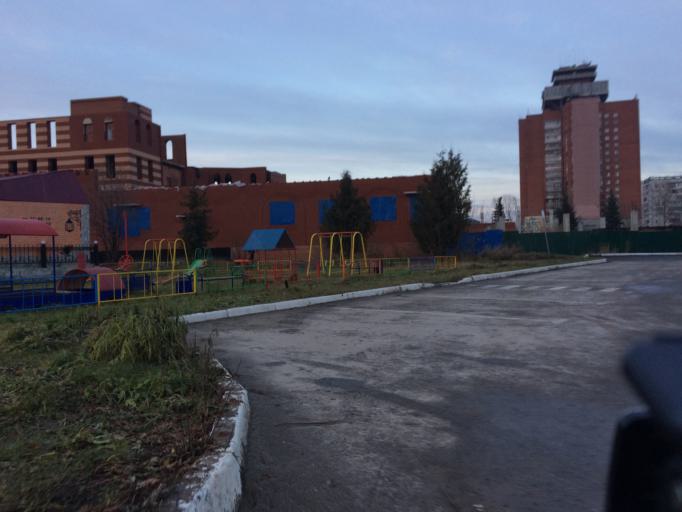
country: RU
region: Mariy-El
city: Yoshkar-Ola
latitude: 56.6259
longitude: 47.9040
